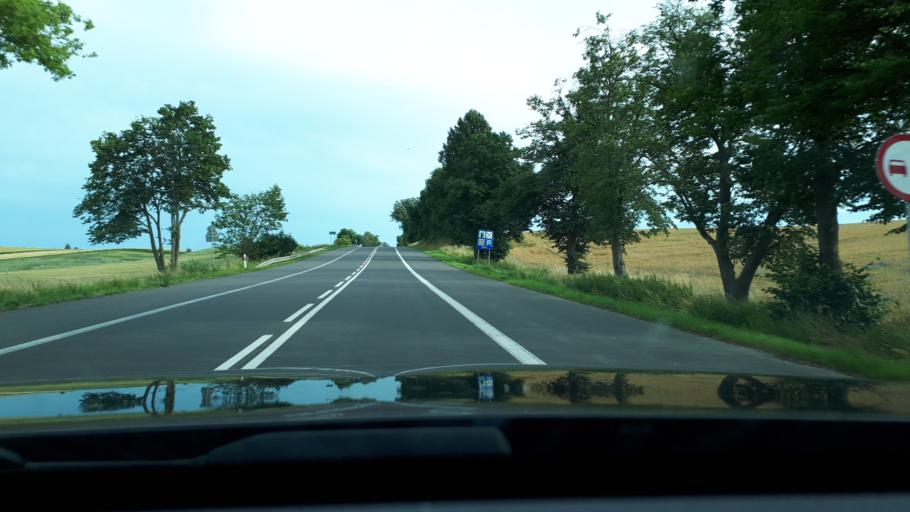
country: PL
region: Warmian-Masurian Voivodeship
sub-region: Powiat ostrodzki
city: Ostroda
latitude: 53.6583
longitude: 20.0498
